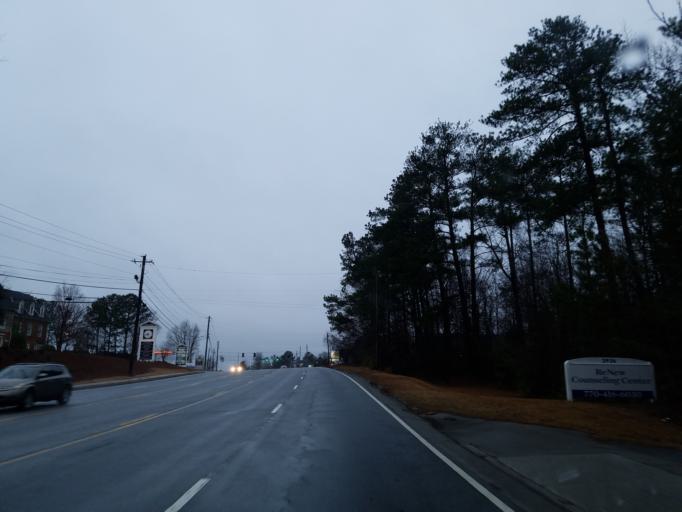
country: US
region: Georgia
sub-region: Gwinnett County
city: Norcross
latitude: 33.9655
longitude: -84.2537
